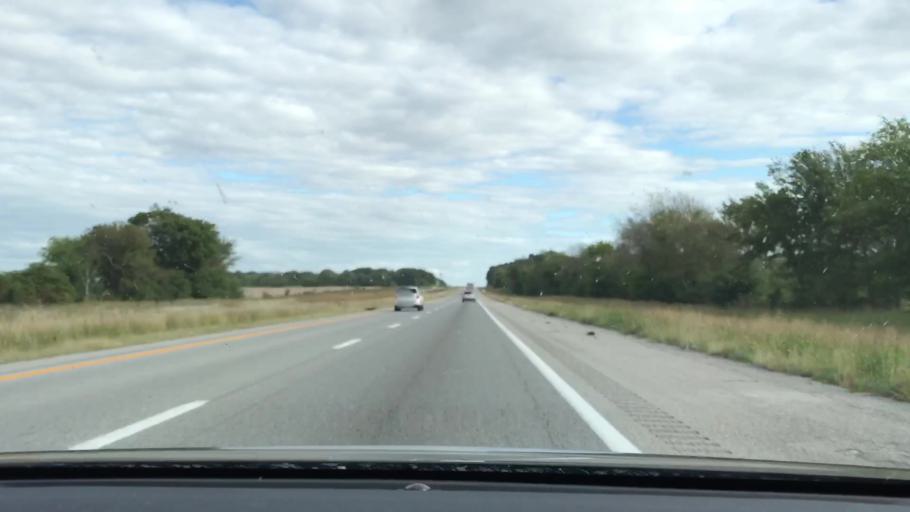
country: US
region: Kentucky
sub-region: Christian County
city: Hopkinsville
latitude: 36.7835
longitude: -87.5787
